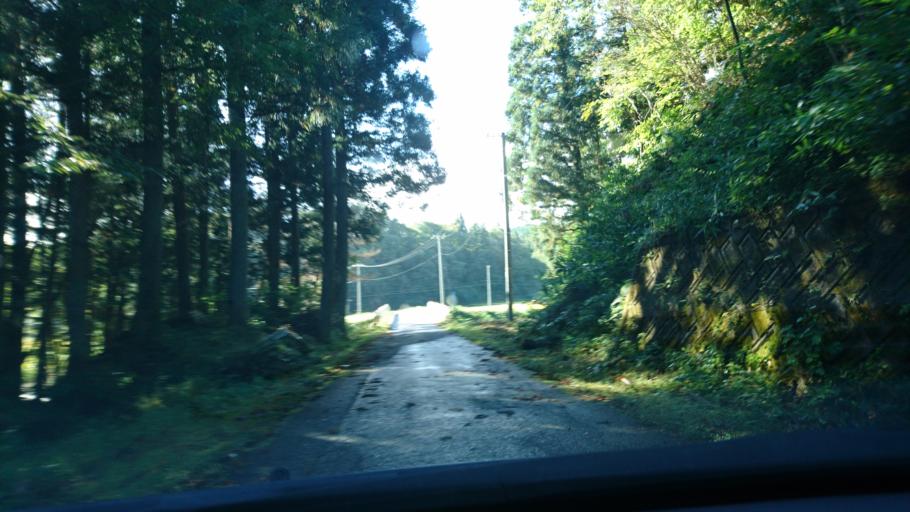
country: JP
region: Iwate
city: Ichinoseki
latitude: 38.9536
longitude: 141.0021
